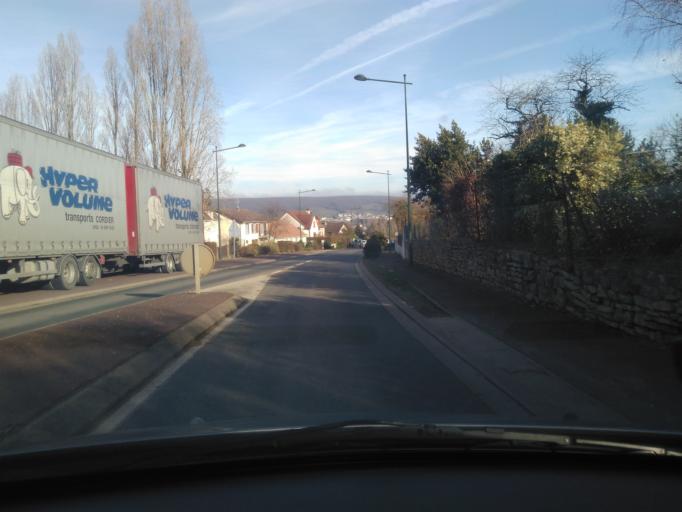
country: FR
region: Centre
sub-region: Departement du Cher
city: Orval
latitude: 46.7196
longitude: 2.4791
